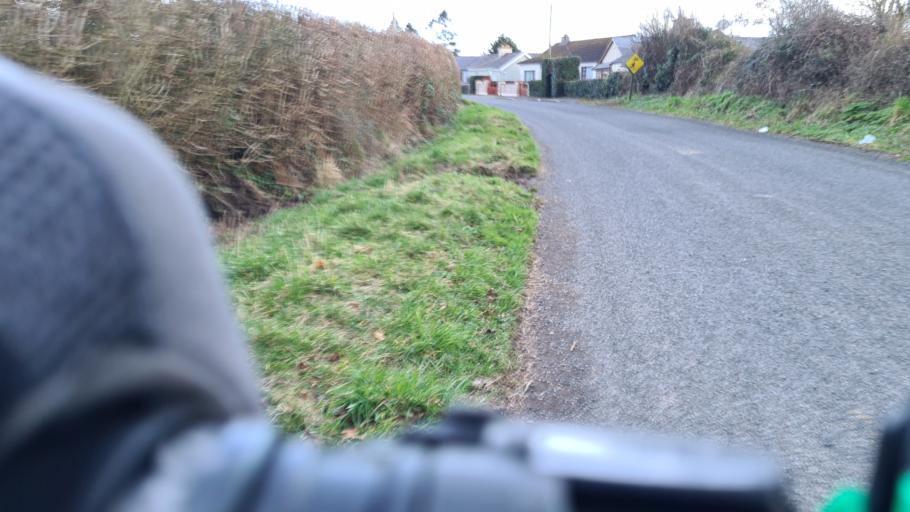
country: IE
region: Leinster
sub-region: Kildare
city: Celbridge
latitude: 53.3355
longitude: -6.5750
